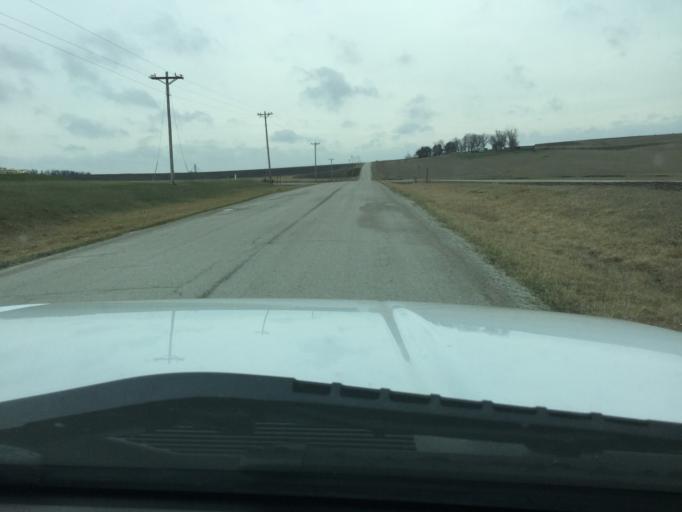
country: US
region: Kansas
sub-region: Nemaha County
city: Sabetha
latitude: 39.8981
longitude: -95.7137
